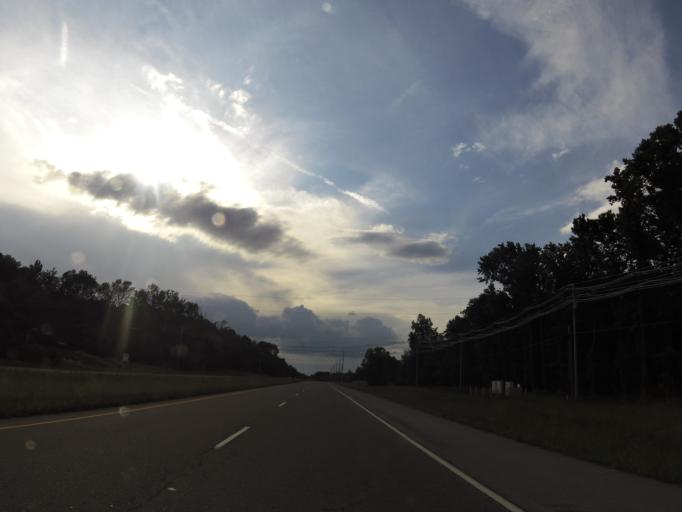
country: US
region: Tennessee
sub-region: Blount County
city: Wildwood
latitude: 35.7516
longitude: -83.8426
